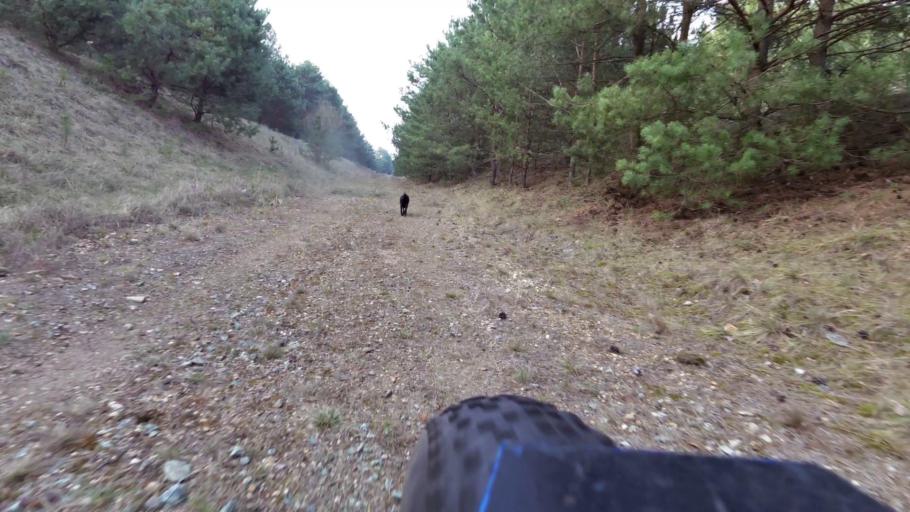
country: DE
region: Brandenburg
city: Vogelsang
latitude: 52.2626
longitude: 14.6921
